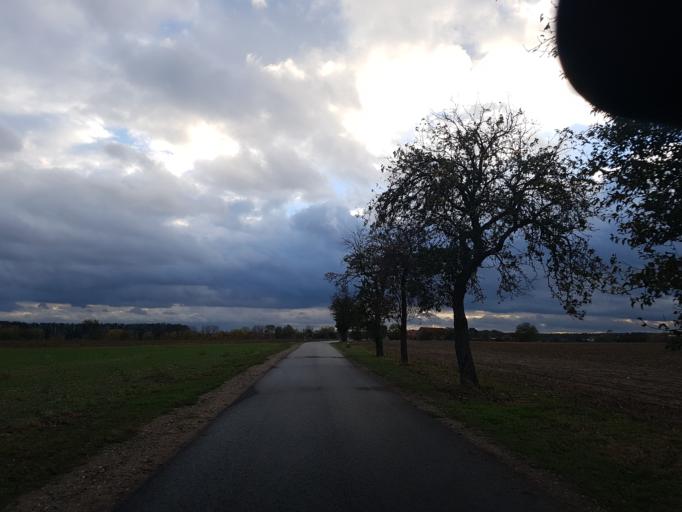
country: DE
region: Saxony-Anhalt
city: Seyda
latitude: 51.8971
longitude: 12.9012
